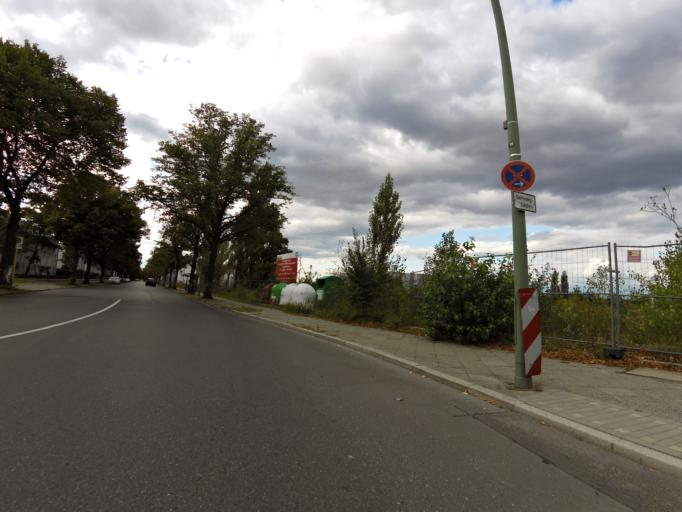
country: DE
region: Berlin
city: Johannisthal
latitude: 52.4241
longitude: 13.5144
